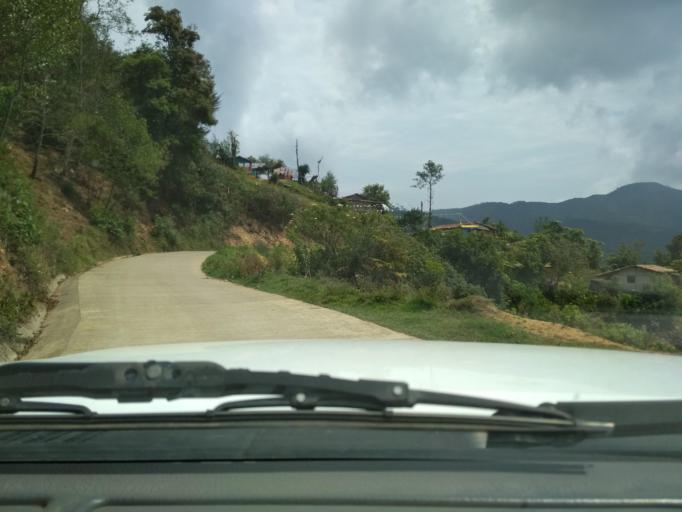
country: MX
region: Veracruz
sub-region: Camerino Z. Mendoza
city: Necoxtla
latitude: 18.7732
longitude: -97.1544
